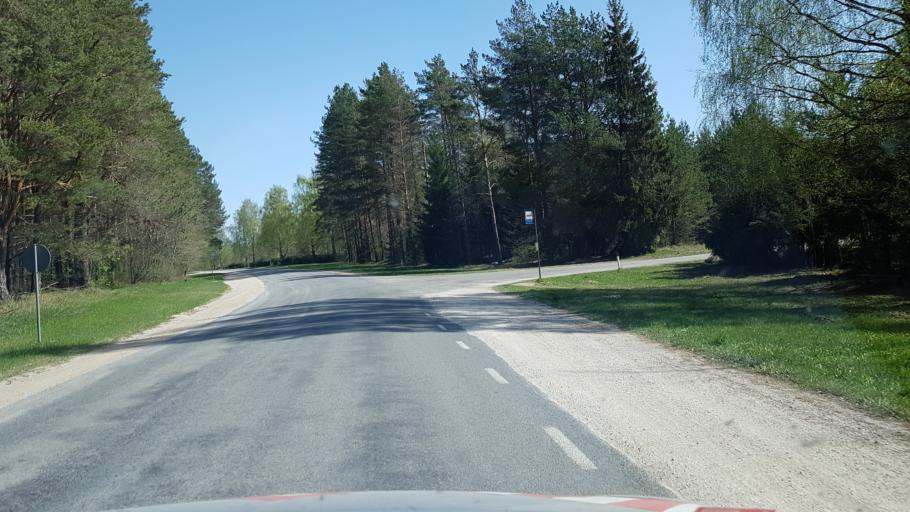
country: EE
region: Tartu
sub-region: Elva linn
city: Elva
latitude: 58.2431
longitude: 26.4367
